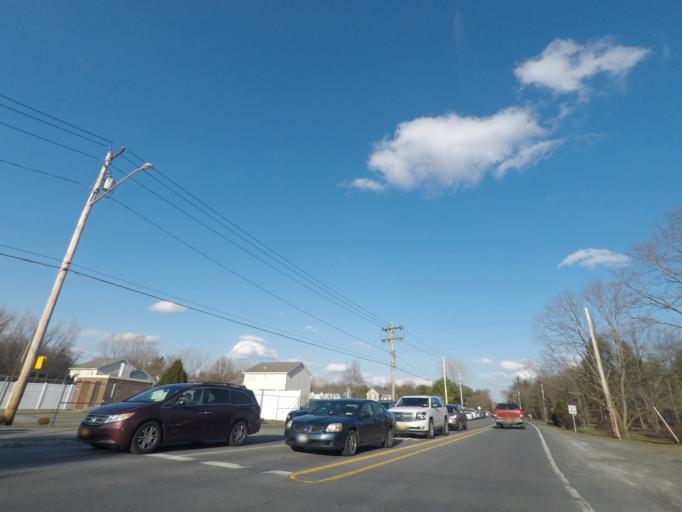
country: US
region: New York
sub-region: Saratoga County
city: Country Knolls
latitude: 42.8549
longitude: -73.7942
